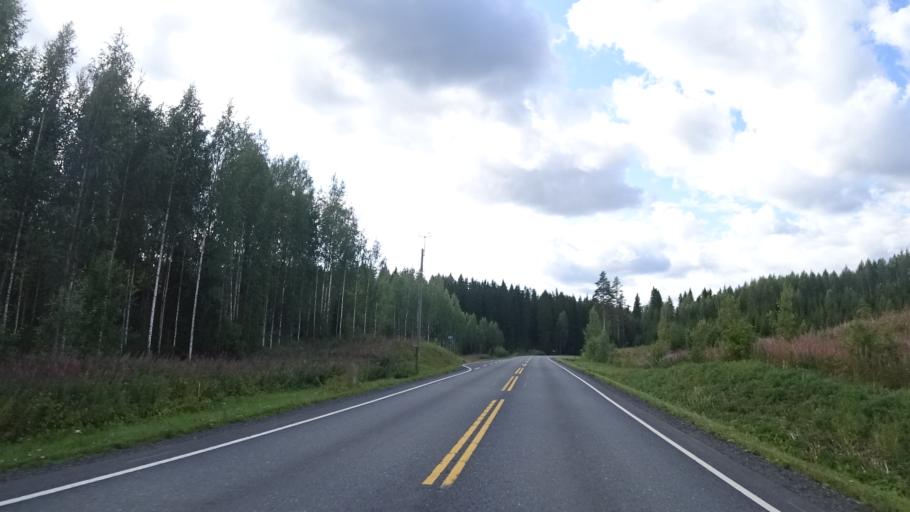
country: FI
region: North Karelia
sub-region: Keski-Karjala
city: Tohmajaervi
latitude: 62.1777
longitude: 30.5267
